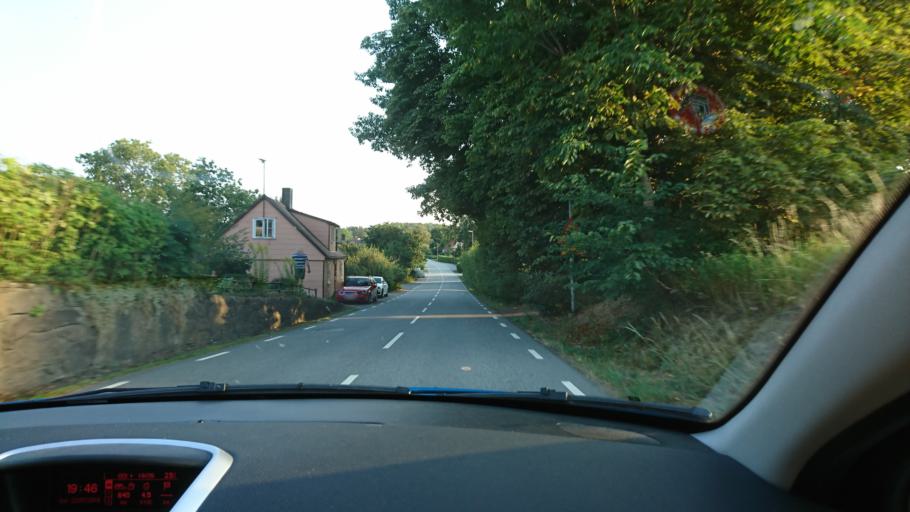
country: SE
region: Skane
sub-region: Simrishamns Kommun
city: Kivik
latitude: 55.7128
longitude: 14.1533
